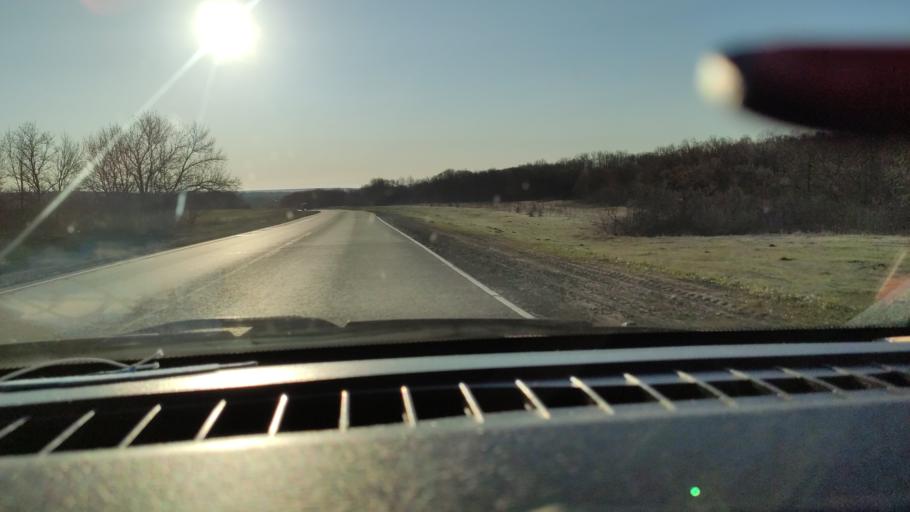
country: RU
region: Saratov
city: Tersa
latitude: 52.1021
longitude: 47.4590
